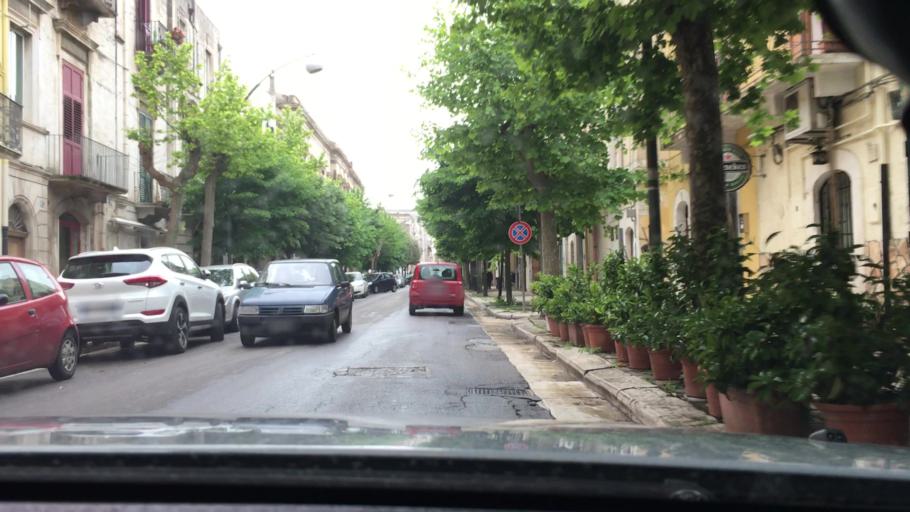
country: IT
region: Apulia
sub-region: Provincia di Bari
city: Gioia del Colle
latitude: 40.8028
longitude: 16.9231
